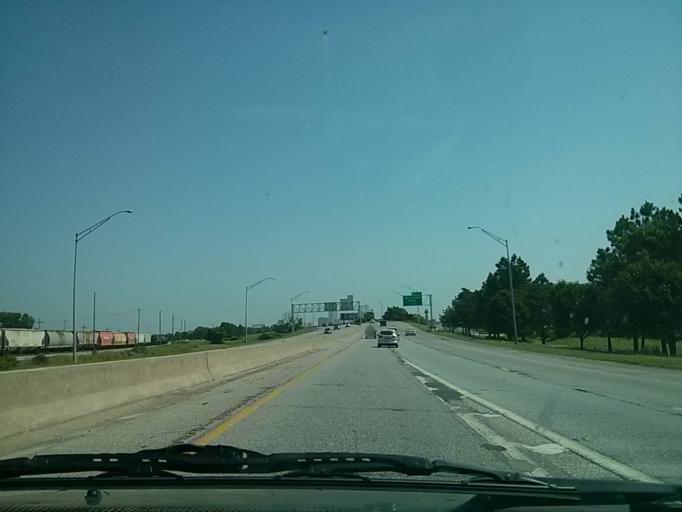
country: US
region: Oklahoma
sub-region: Tulsa County
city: Tulsa
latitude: 36.1154
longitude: -96.0105
